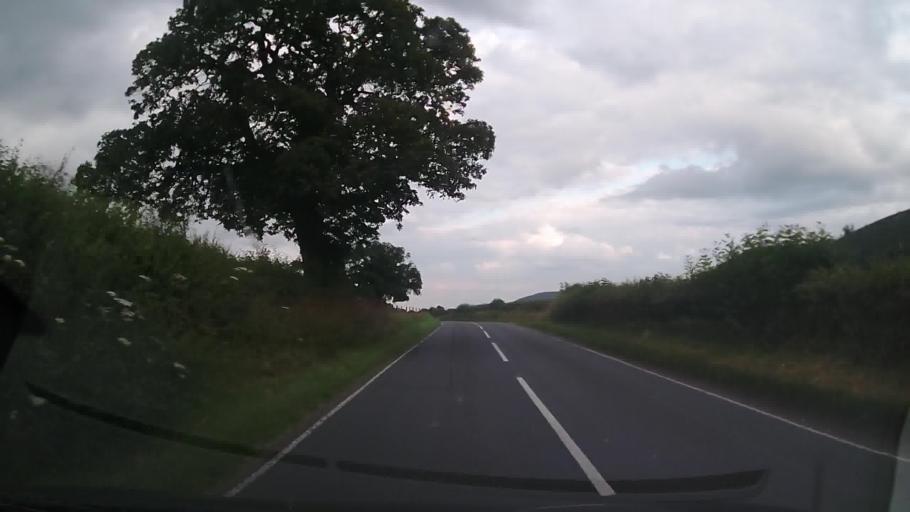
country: GB
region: Wales
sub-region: Sir Powys
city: Llanrhaeadr-ym-Mochnant
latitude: 52.8129
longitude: -3.2600
